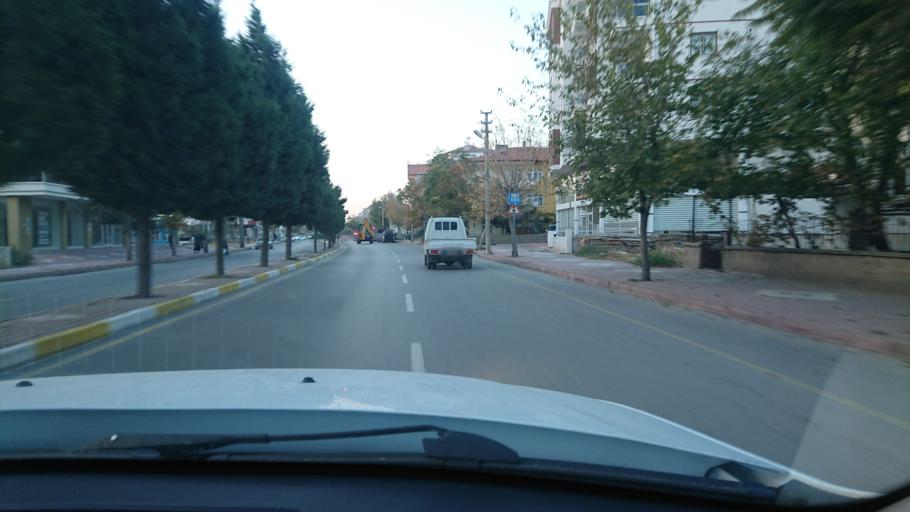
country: TR
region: Aksaray
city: Aksaray
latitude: 38.3624
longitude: 34.0364
